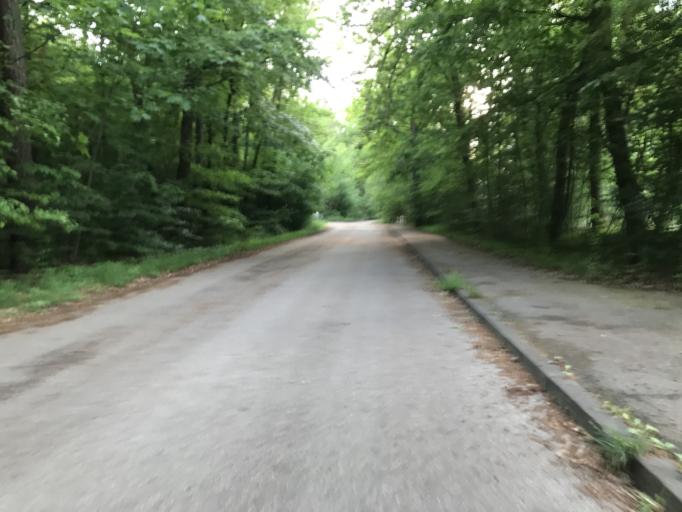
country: DE
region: Baden-Wuerttemberg
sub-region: Regierungsbezirk Stuttgart
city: Stuttgart Feuerbach
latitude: 48.8296
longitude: 9.1473
